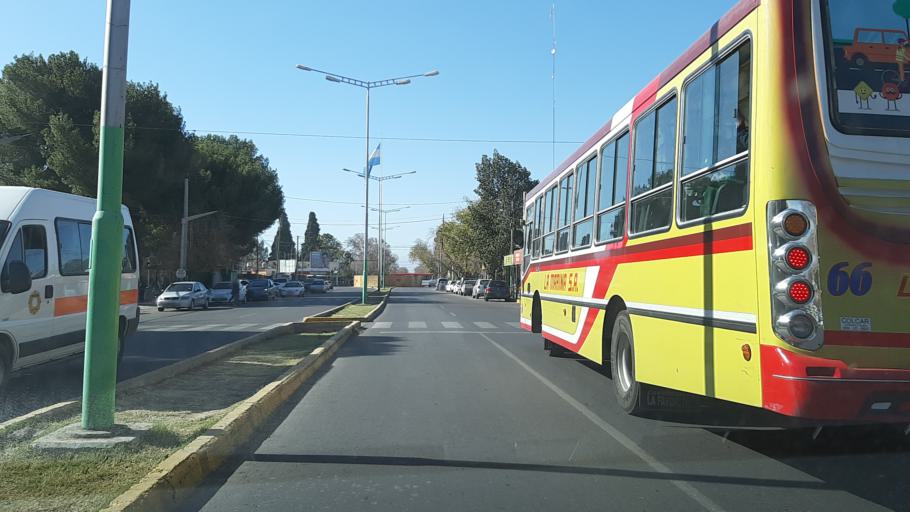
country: AR
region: San Juan
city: San Juan
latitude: -31.5308
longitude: -68.5963
